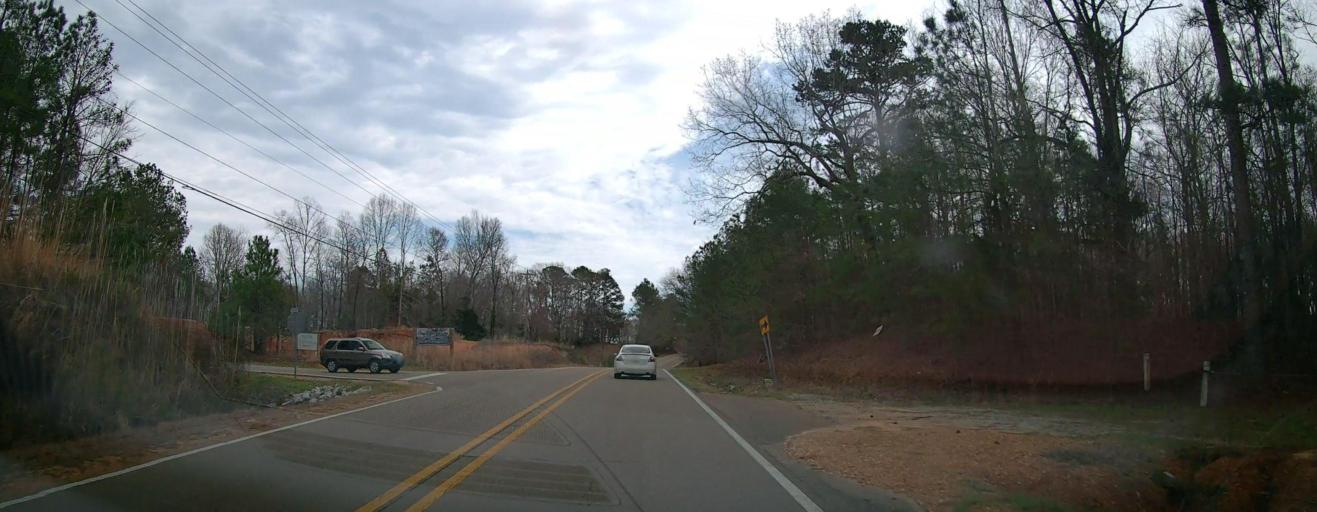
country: US
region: Mississippi
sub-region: Itawamba County
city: Fulton
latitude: 34.2747
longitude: -88.3477
